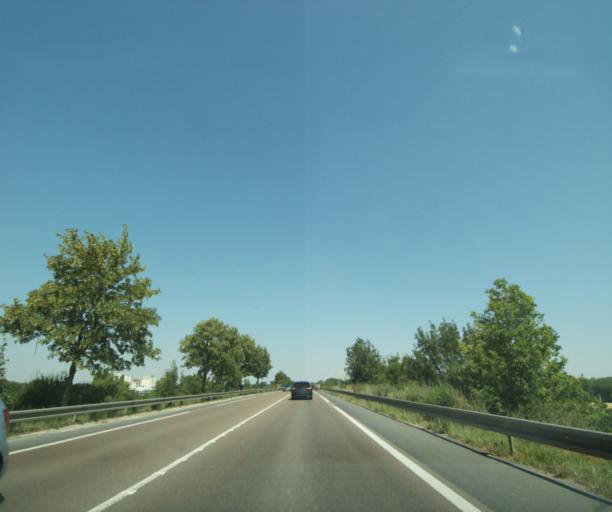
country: FR
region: Champagne-Ardenne
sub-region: Departement de la Marne
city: Frignicourt
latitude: 48.7214
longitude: 4.6296
